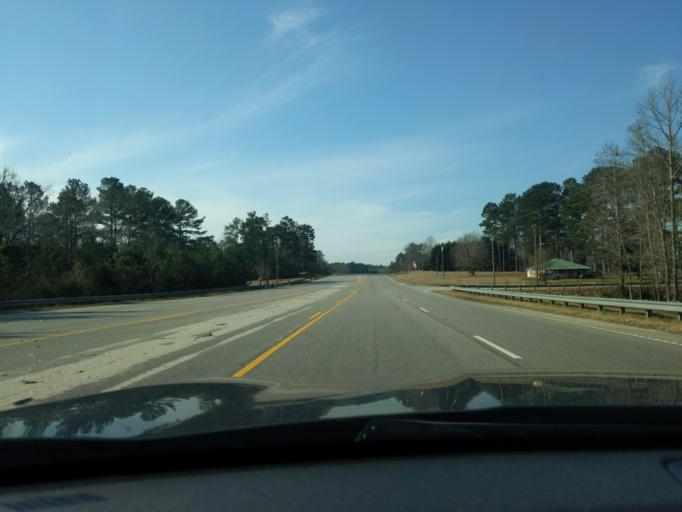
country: US
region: South Carolina
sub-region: Abbeville County
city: Abbeville
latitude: 34.1401
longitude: -82.4089
